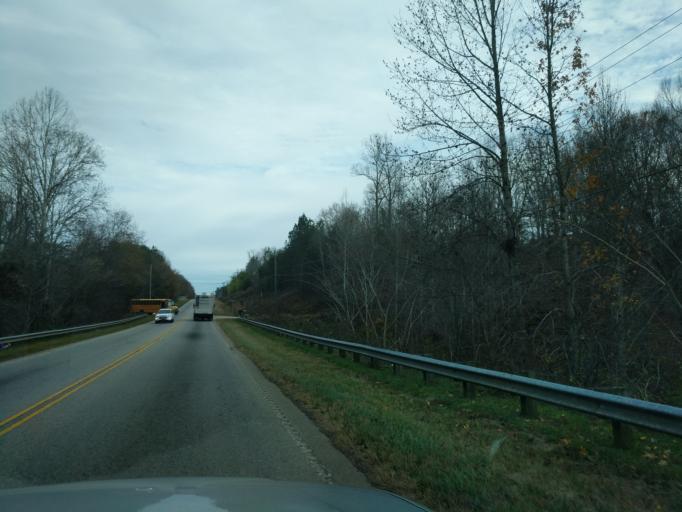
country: US
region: South Carolina
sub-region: Anderson County
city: Williamston
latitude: 34.6425
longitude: -82.4493
